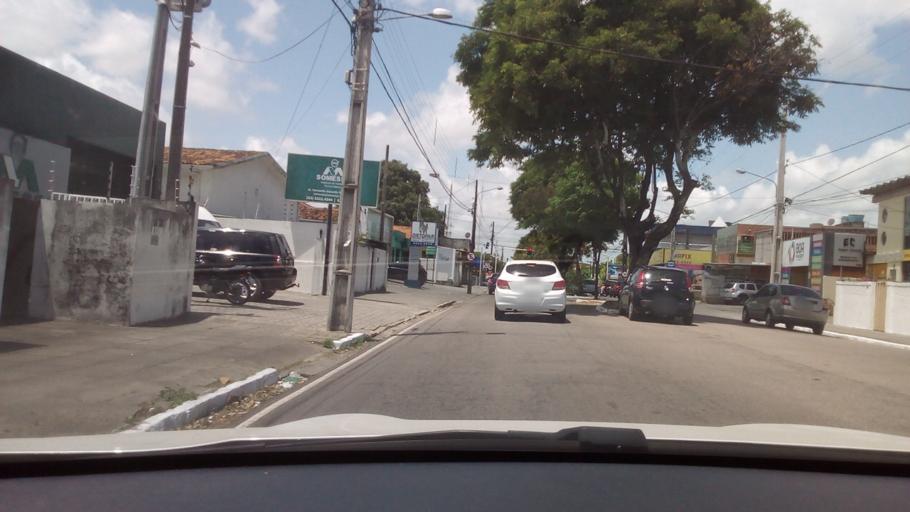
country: BR
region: Paraiba
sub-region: Joao Pessoa
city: Joao Pessoa
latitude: -7.1261
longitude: -34.8699
